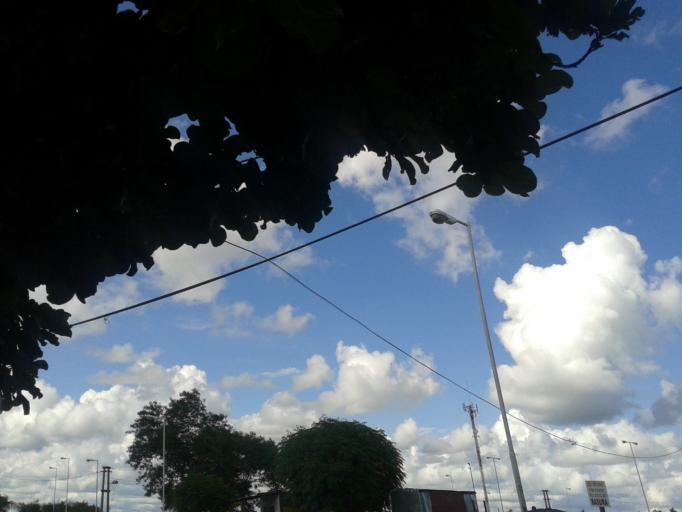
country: AR
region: Formosa
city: Clorinda
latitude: -25.2828
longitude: -57.7343
